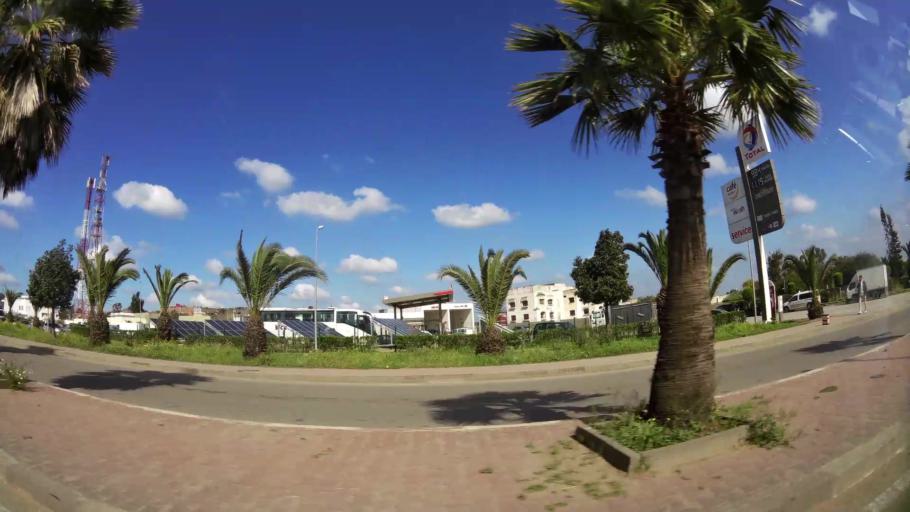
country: MA
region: Grand Casablanca
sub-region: Mediouna
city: Mediouna
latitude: 33.4540
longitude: -7.5218
